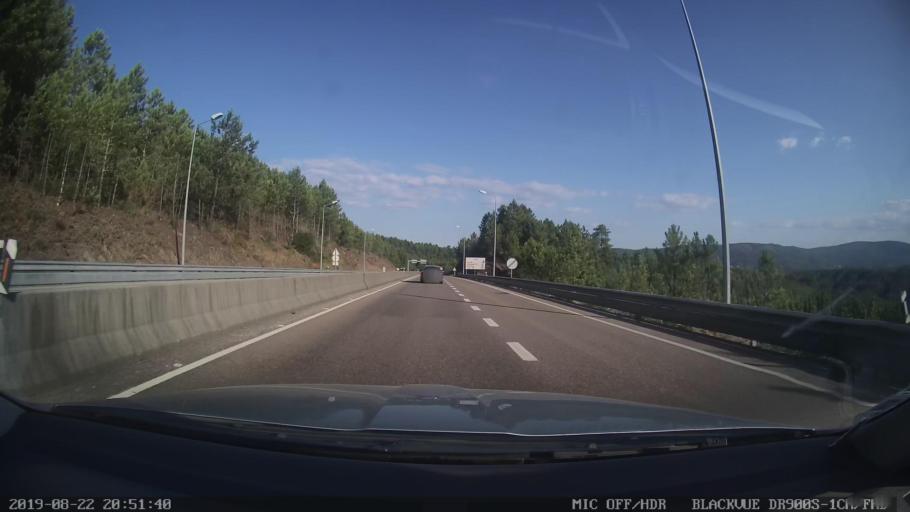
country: PT
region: Castelo Branco
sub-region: Proenca-A-Nova
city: Proenca-a-Nova
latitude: 39.7614
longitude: -7.9638
